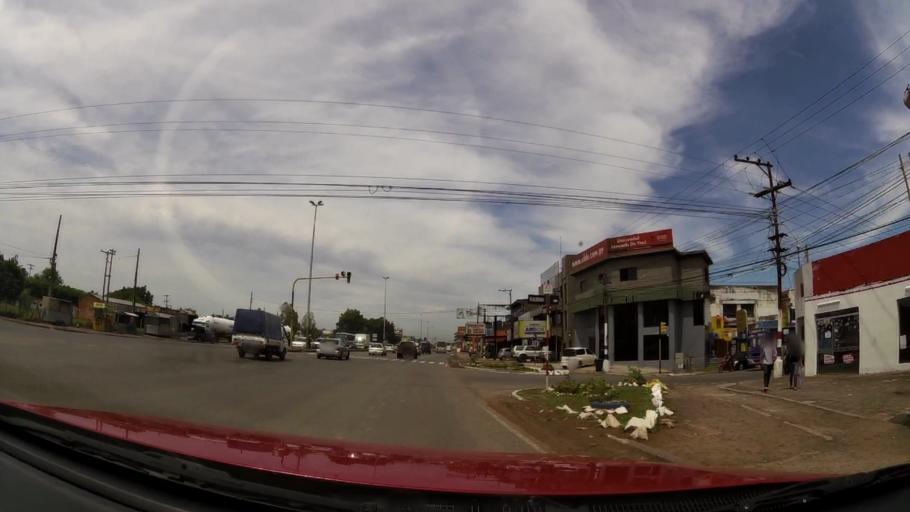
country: PY
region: Central
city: Colonia Mariano Roque Alonso
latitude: -25.2129
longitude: -57.5293
